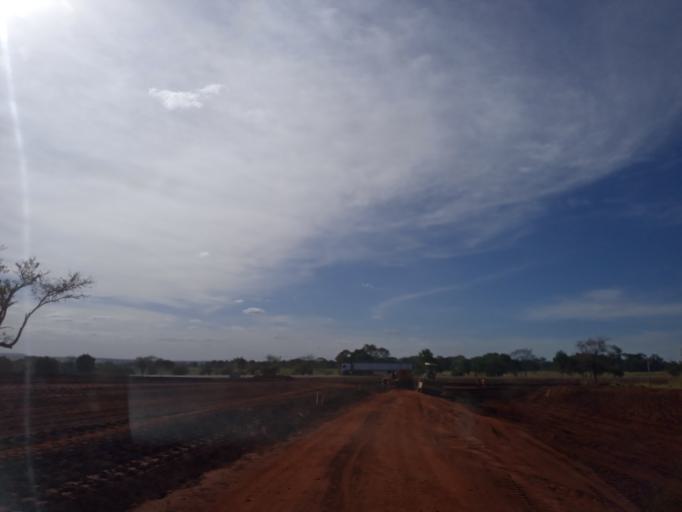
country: BR
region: Minas Gerais
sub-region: Ituiutaba
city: Ituiutaba
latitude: -18.9668
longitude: -49.5063
